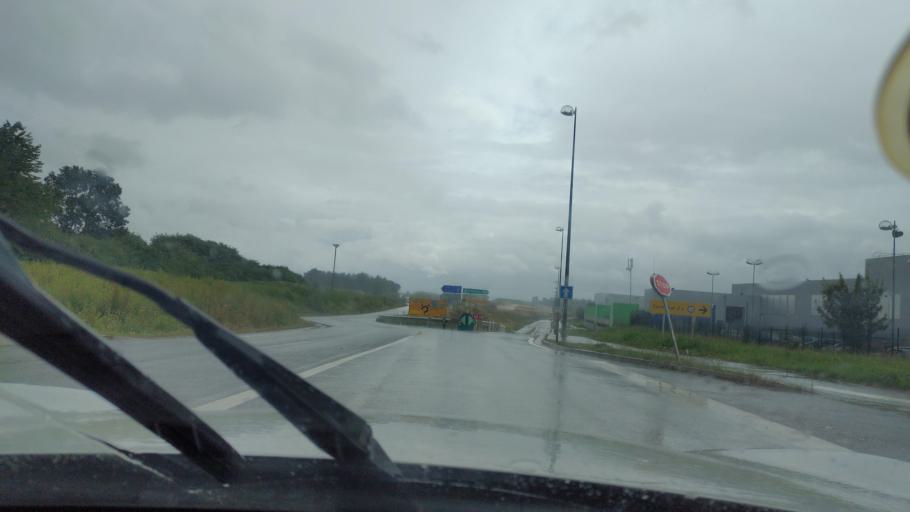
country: FR
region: Ile-de-France
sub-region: Departement de Seine-et-Marne
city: Mitry-Mory
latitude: 49.0127
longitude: 2.5888
